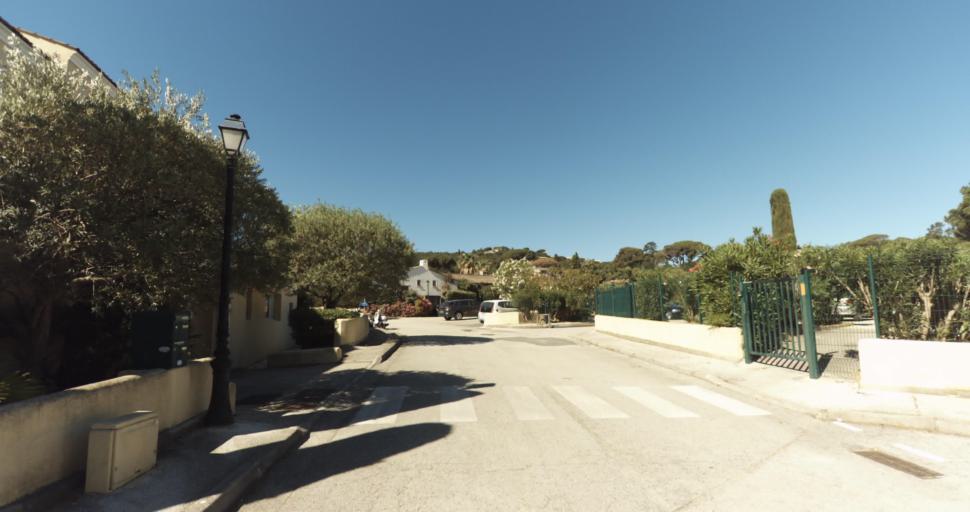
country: FR
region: Provence-Alpes-Cote d'Azur
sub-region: Departement du Var
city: Saint-Tropez
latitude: 43.2618
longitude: 6.6190
